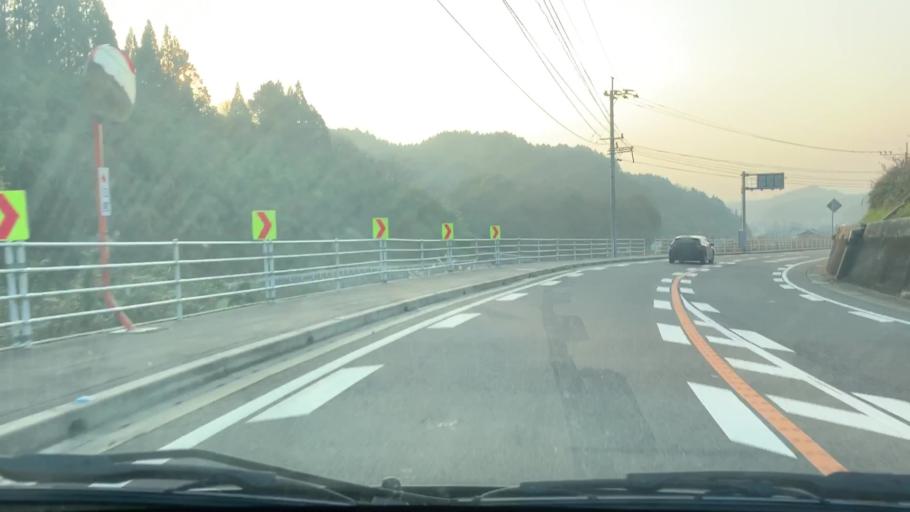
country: JP
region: Saga Prefecture
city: Takeocho-takeo
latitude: 33.2551
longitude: 130.0158
